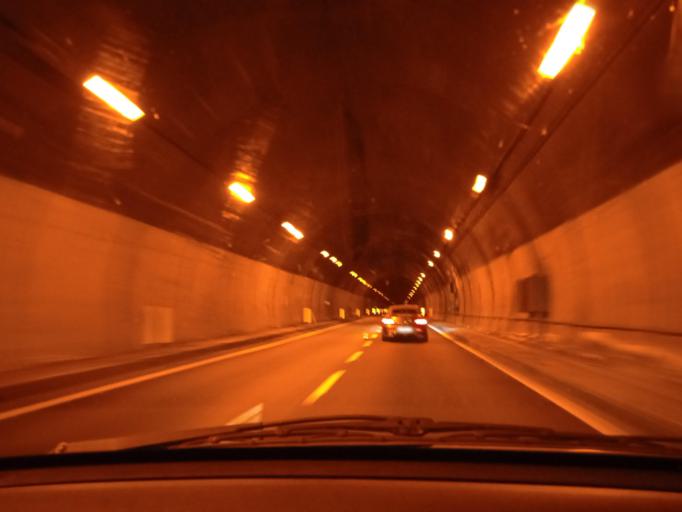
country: IT
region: Sicily
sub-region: Messina
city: Gioiosa Marea
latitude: 38.1568
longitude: 14.9026
